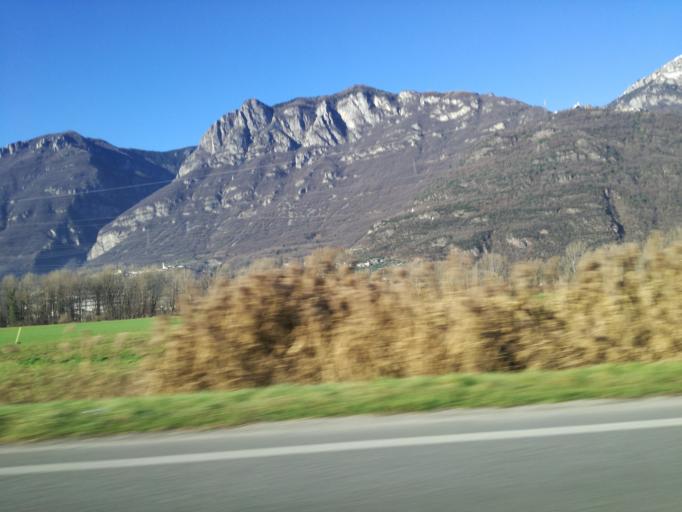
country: IT
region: Lombardy
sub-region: Provincia di Brescia
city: Pian Camuno
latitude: 45.8446
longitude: 10.1353
